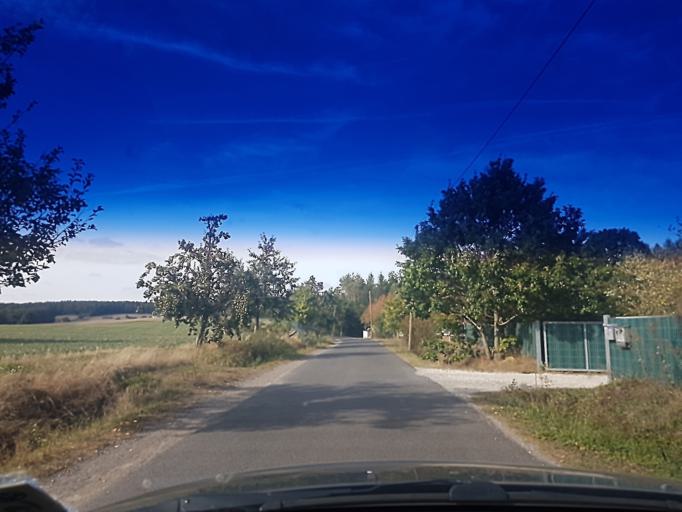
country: DE
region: Bavaria
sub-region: Upper Franconia
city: Burgwindheim
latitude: 49.7779
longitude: 10.5441
